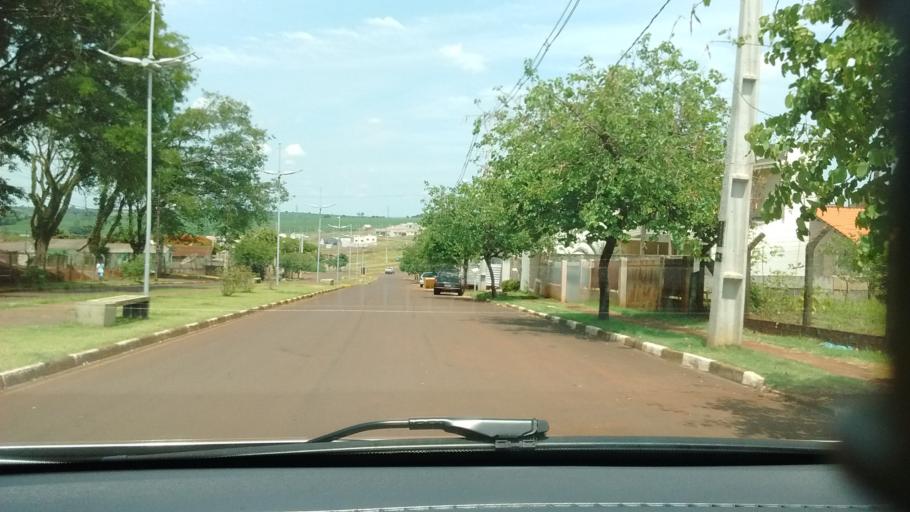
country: BR
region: Parana
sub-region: Corbelia
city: Corbelia
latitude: -24.5501
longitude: -52.9836
